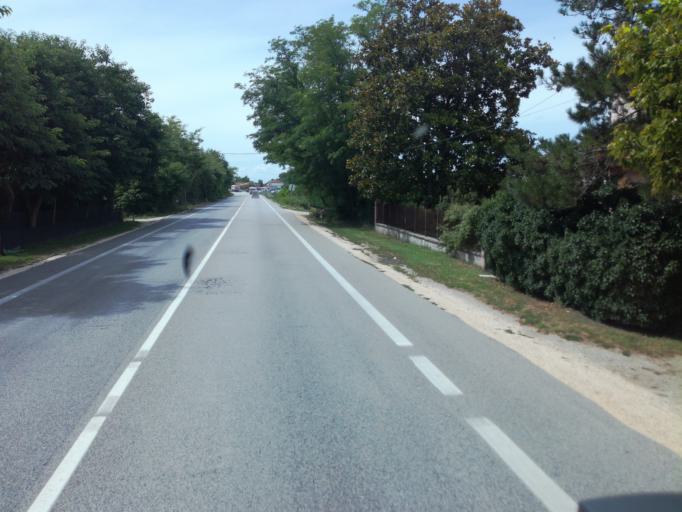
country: IT
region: Veneto
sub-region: Provincia di Rovigo
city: Rosolina
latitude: 45.0934
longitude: 12.2532
